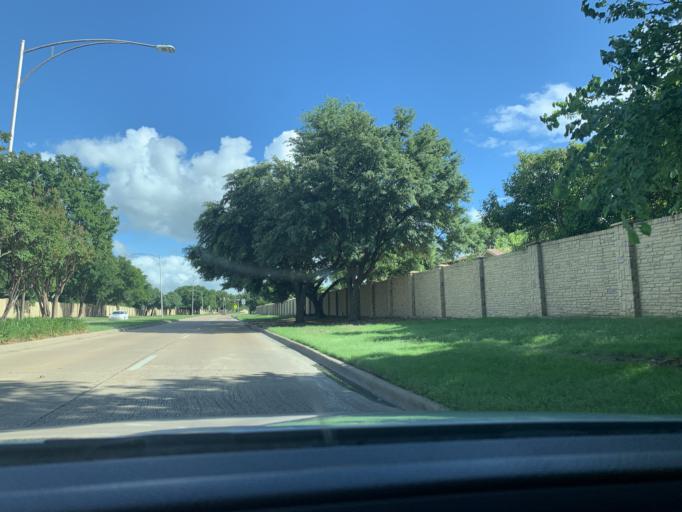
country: US
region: Texas
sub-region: Dallas County
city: Grand Prairie
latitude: 32.6656
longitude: -97.0429
